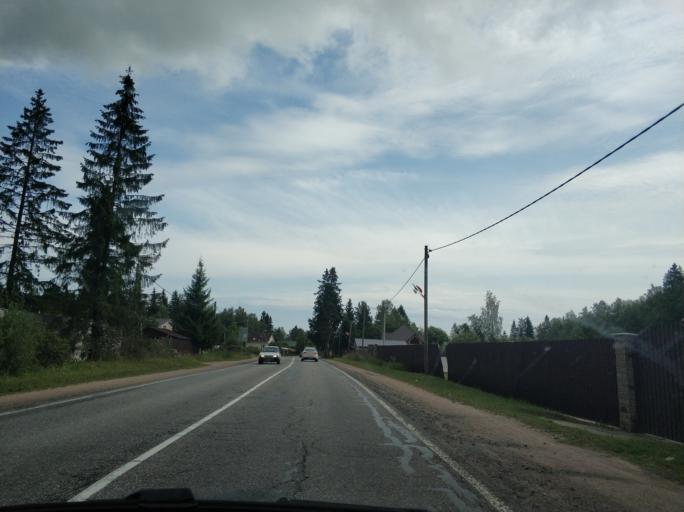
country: RU
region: Leningrad
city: Borisova Griva
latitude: 60.0895
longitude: 30.9531
